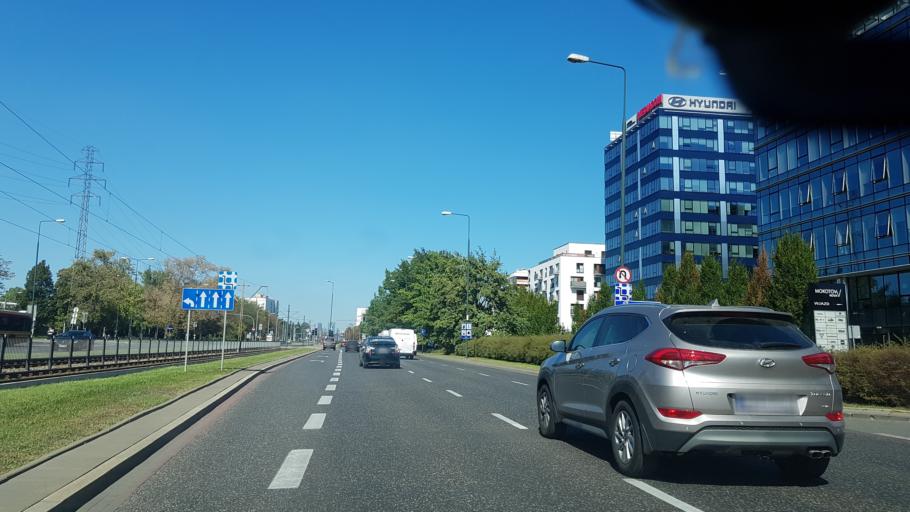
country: PL
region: Masovian Voivodeship
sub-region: Warszawa
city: Mokotow
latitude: 52.1845
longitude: 21.0023
